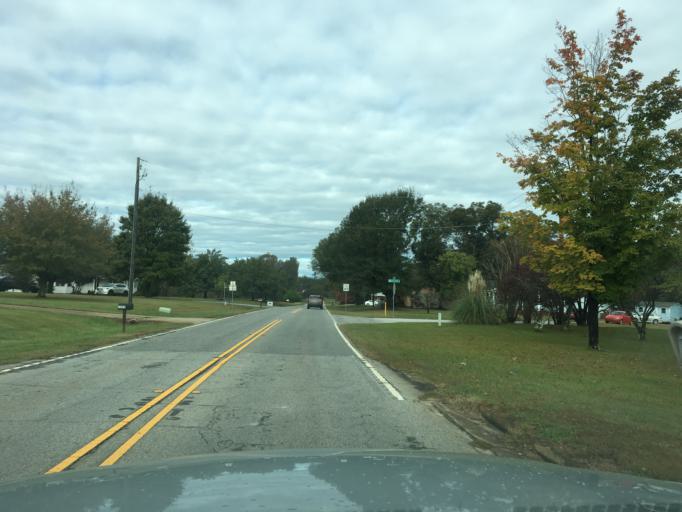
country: US
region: South Carolina
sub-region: Greenville County
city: Greer
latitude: 34.9725
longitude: -82.2009
